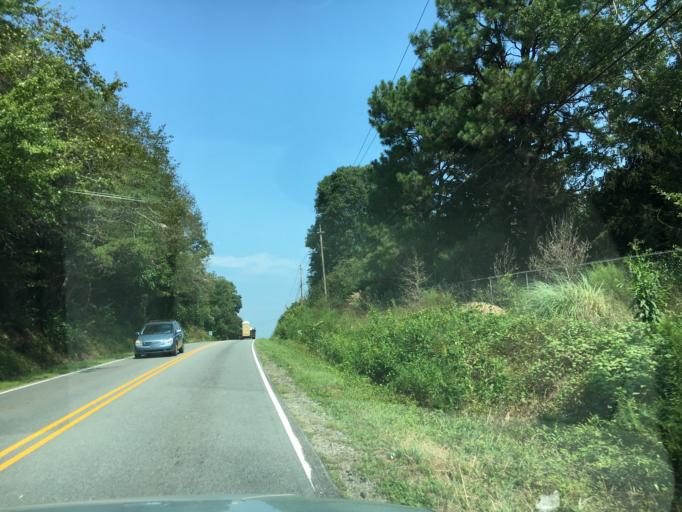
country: US
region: North Carolina
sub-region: Rutherford County
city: Rutherfordton
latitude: 35.3456
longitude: -81.9633
